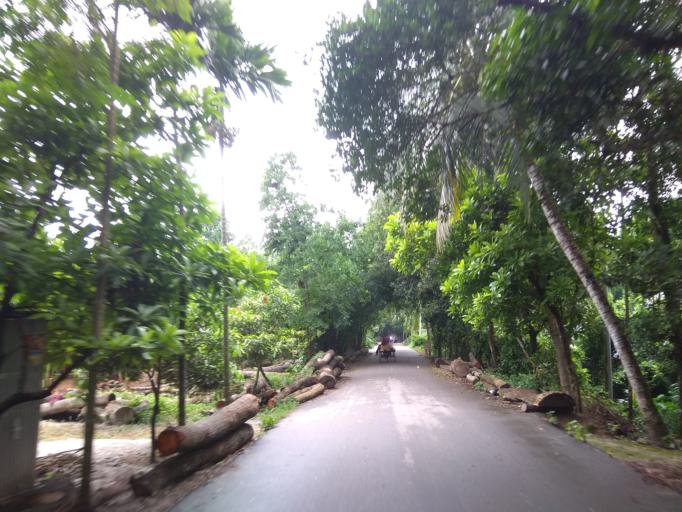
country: BD
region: Dhaka
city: Dohar
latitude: 23.4364
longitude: 90.0735
